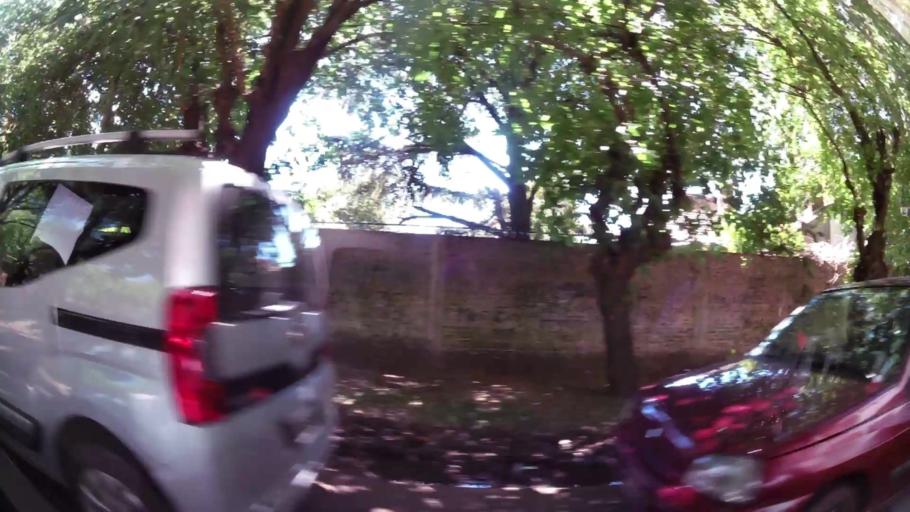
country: AR
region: Buenos Aires
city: Hurlingham
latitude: -34.4988
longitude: -58.6431
